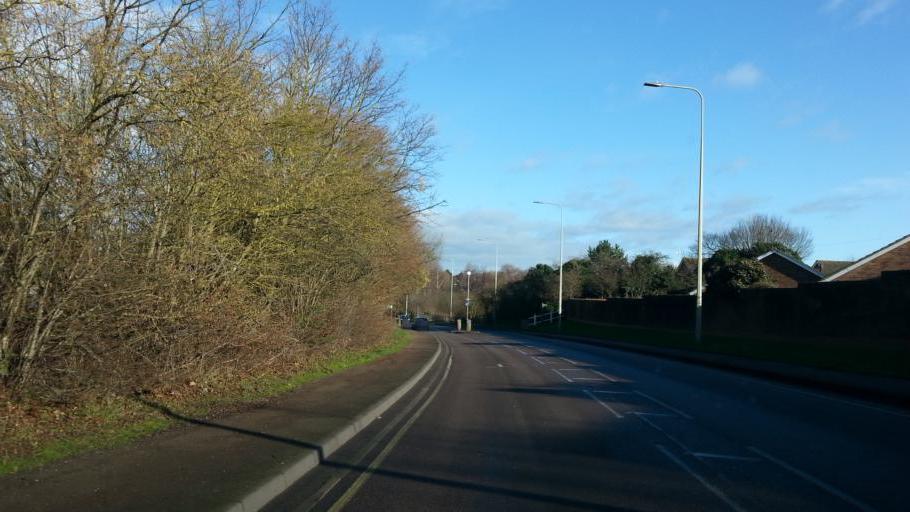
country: GB
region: England
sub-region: Suffolk
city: Halesworth
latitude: 52.3403
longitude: 1.5028
